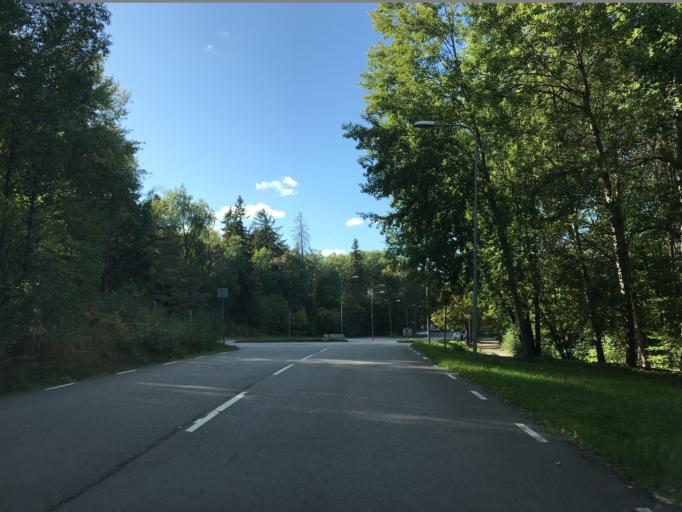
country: SE
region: Stockholm
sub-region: Huddinge Kommun
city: Segeltorp
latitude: 59.2852
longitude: 17.8953
